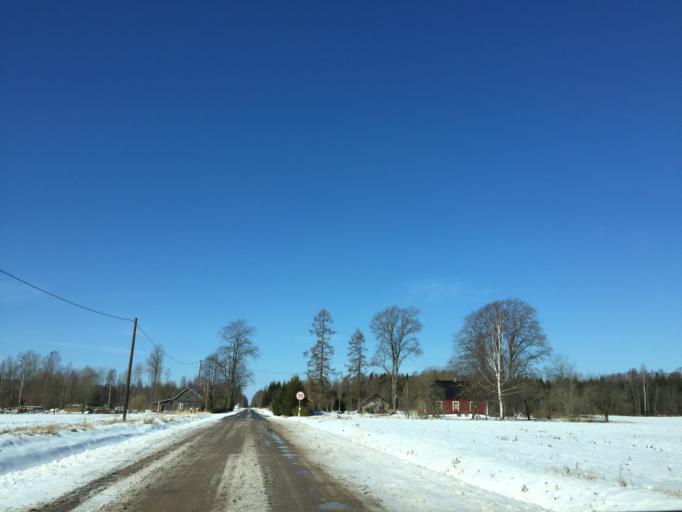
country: LV
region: Aloja
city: Staicele
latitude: 58.0269
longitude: 24.5725
